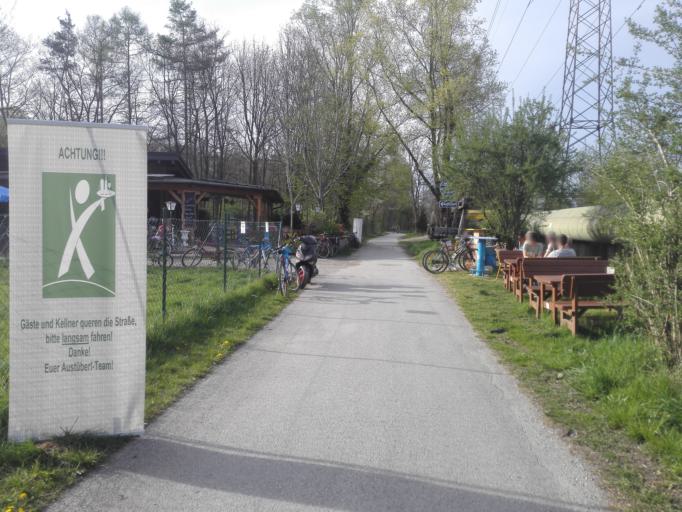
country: AT
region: Styria
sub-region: Politischer Bezirk Graz-Umgebung
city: Feldkirchen bei Graz
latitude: 47.0175
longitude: 15.4571
